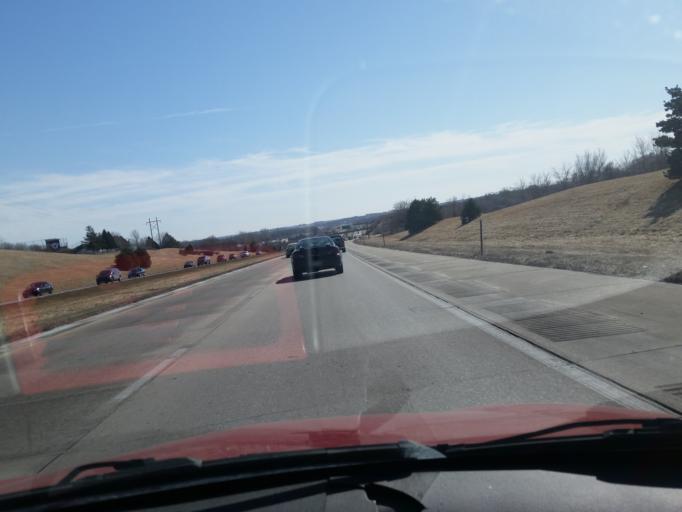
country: US
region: Nebraska
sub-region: Sarpy County
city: Offutt Air Force Base
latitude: 41.1676
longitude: -95.9393
